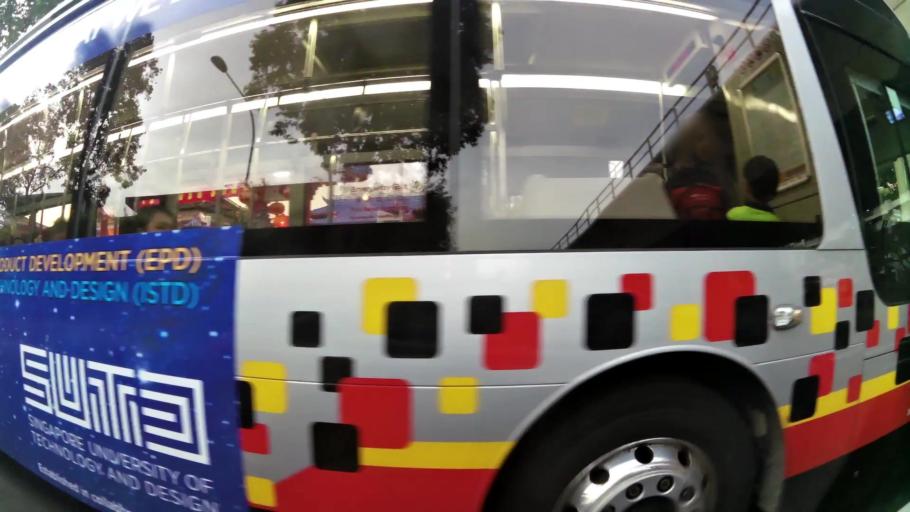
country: MY
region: Johor
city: Kampung Pasir Gudang Baru
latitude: 1.4346
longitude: 103.8342
